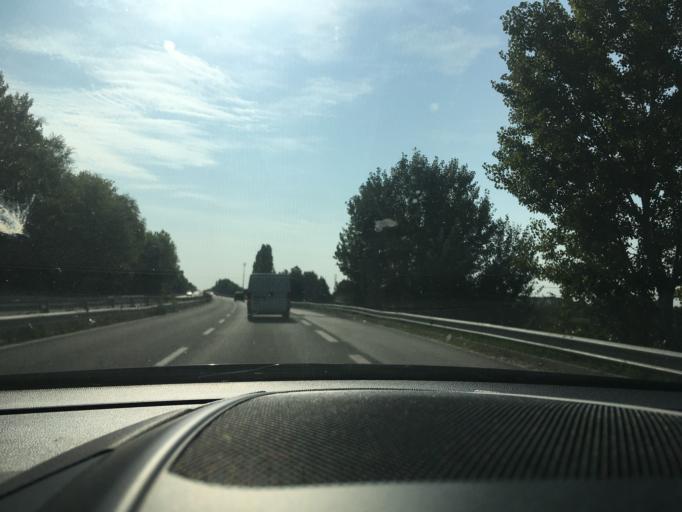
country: IT
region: Emilia-Romagna
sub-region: Forli-Cesena
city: San Mauro a Mare
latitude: 44.1495
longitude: 12.4447
